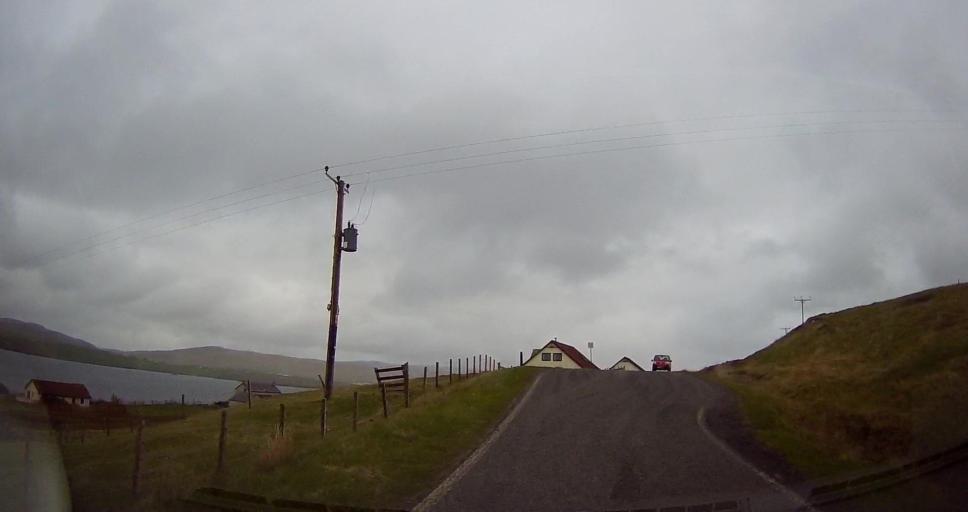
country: GB
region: Scotland
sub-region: Shetland Islands
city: Lerwick
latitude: 60.3838
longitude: -1.3795
